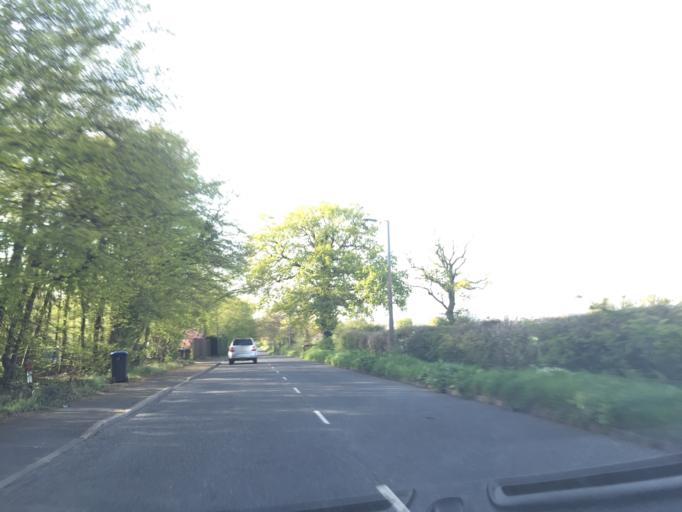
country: GB
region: England
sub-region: Essex
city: Harlow
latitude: 51.7427
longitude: 0.0978
